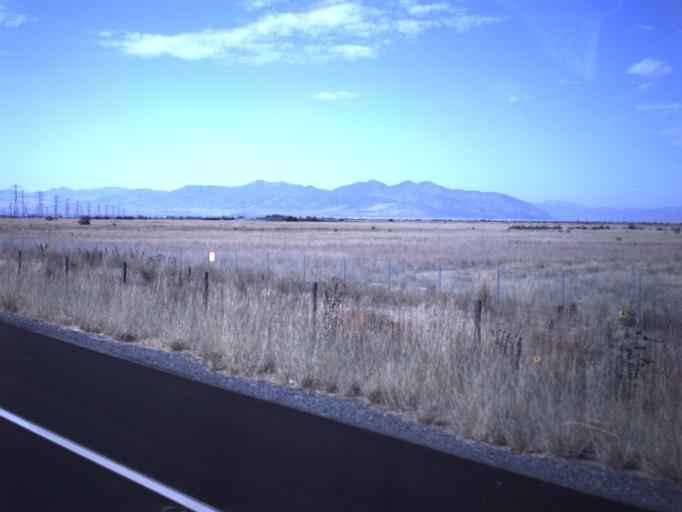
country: US
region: Utah
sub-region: Davis County
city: West Bountiful
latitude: 40.8769
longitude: -111.9381
